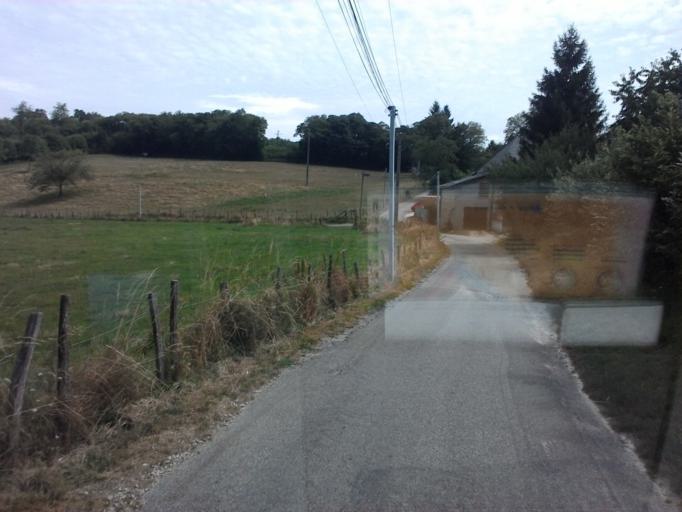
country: FR
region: Rhone-Alpes
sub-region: Departement de l'Isere
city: Montferrat
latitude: 45.5042
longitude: 5.5715
